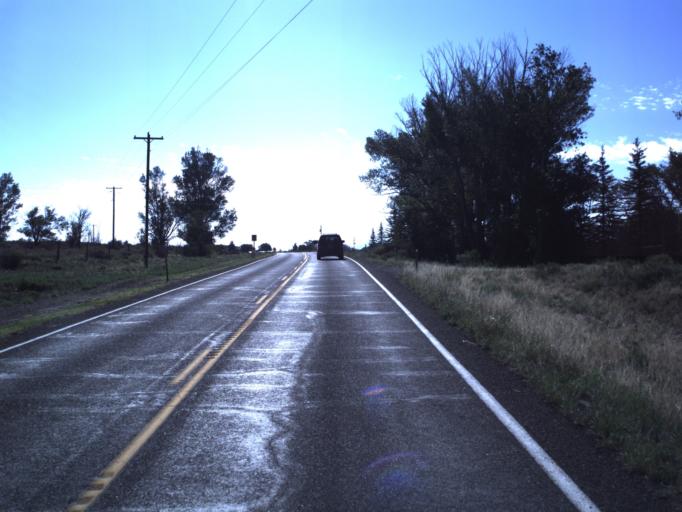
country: US
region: Utah
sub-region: Wayne County
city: Loa
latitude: 38.3004
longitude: -111.4446
